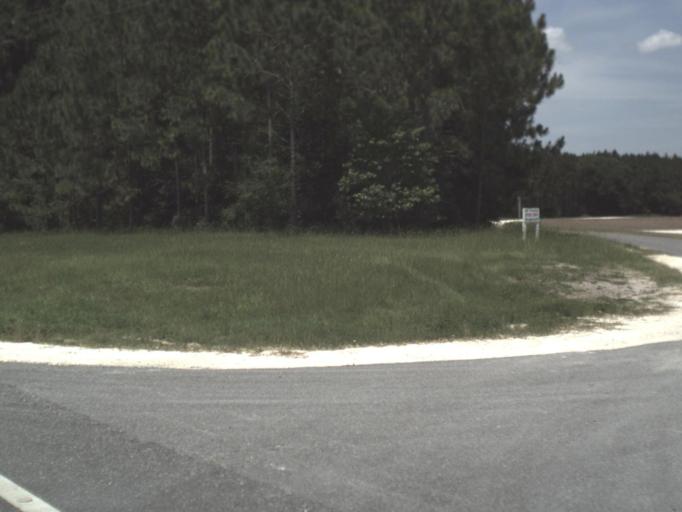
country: US
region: Florida
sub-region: Gilchrist County
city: Trenton
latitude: 29.8308
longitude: -82.8673
